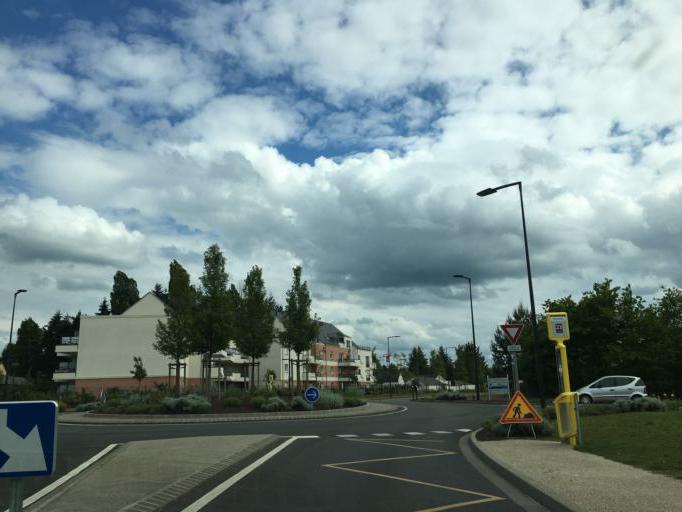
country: FR
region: Centre
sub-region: Departement du Loiret
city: Saint-Pryve-Saint-Mesmin
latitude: 47.8667
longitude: 1.8734
